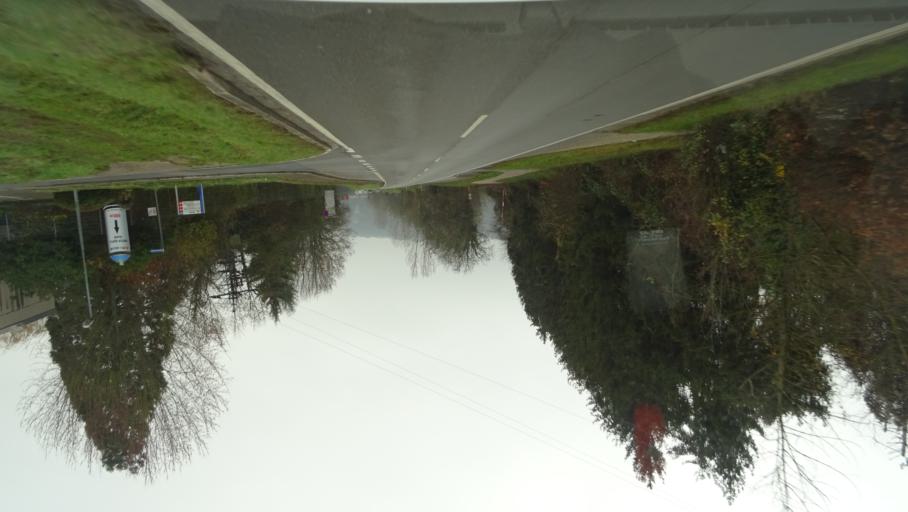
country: DE
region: Baden-Wuerttemberg
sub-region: Karlsruhe Region
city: Hassmersheim
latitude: 49.3096
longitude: 9.1446
